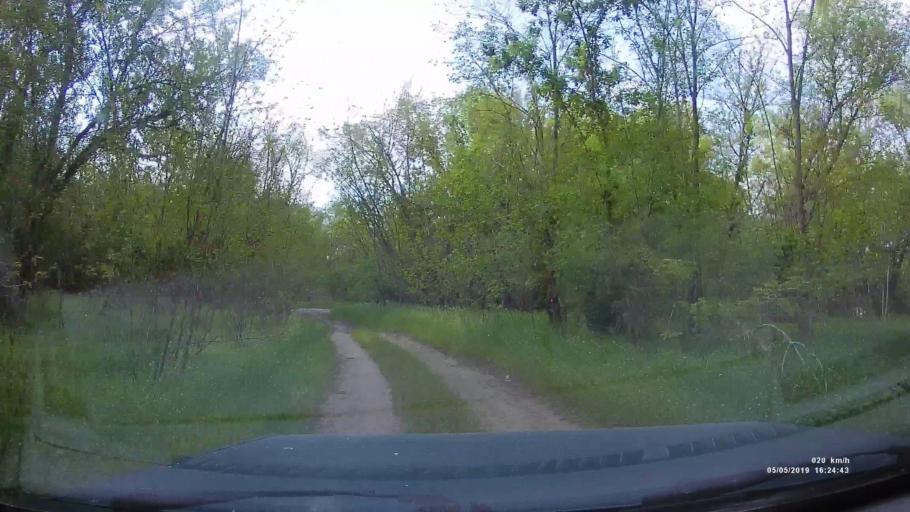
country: RU
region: Rostov
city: Konstantinovsk
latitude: 47.7603
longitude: 41.0250
